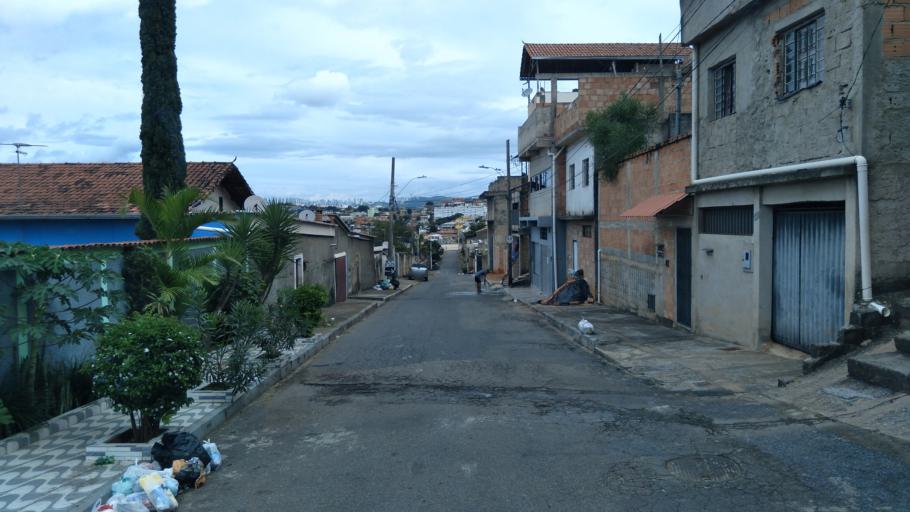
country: BR
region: Minas Gerais
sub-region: Contagem
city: Contagem
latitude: -19.9115
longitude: -44.0060
